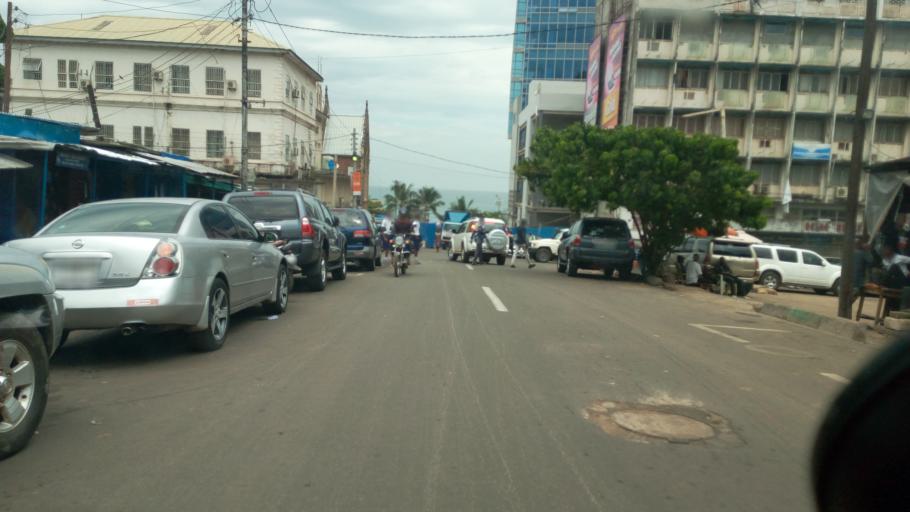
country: SL
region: Western Area
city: Freetown
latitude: 8.4893
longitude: -13.2349
